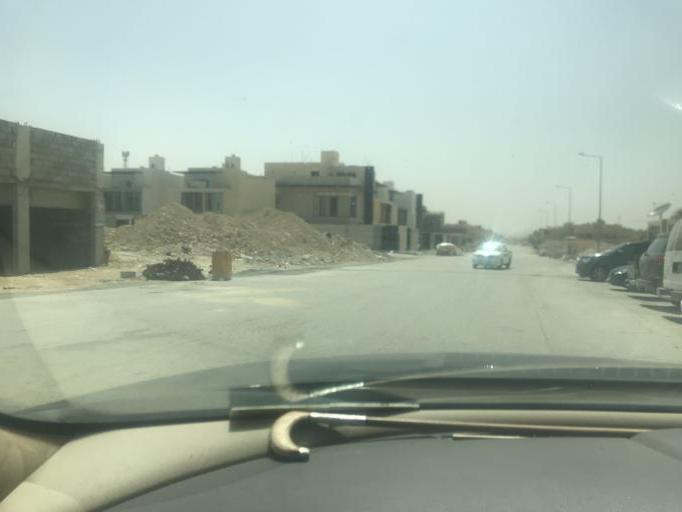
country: SA
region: Ar Riyad
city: Riyadh
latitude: 24.7866
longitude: 46.5874
